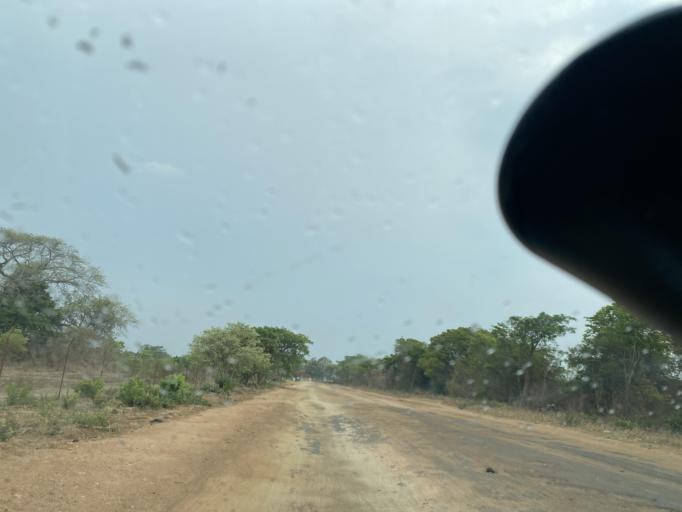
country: ZM
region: Lusaka
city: Lusaka
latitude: -15.2830
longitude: 28.2985
